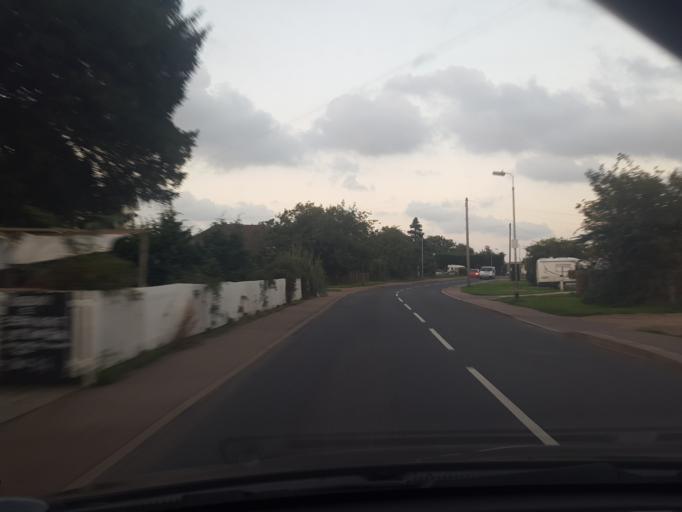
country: GB
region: England
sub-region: Essex
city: Clacton-on-Sea
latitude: 51.8123
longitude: 1.1712
